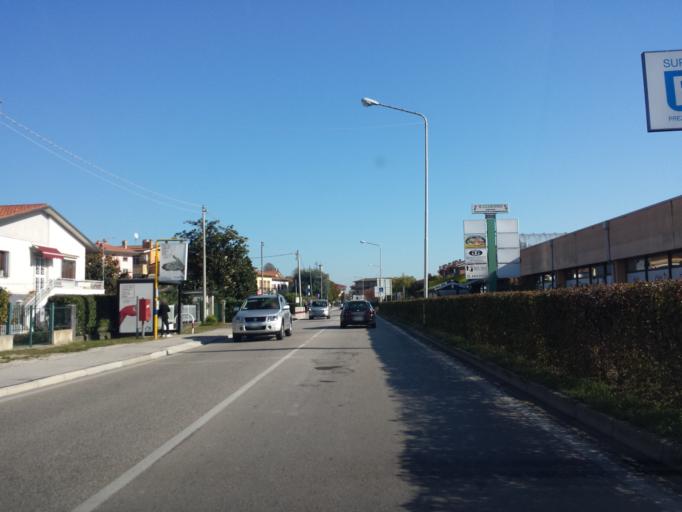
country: IT
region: Veneto
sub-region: Provincia di Vicenza
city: Villaggio Montegrappa
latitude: 45.5407
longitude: 11.5963
